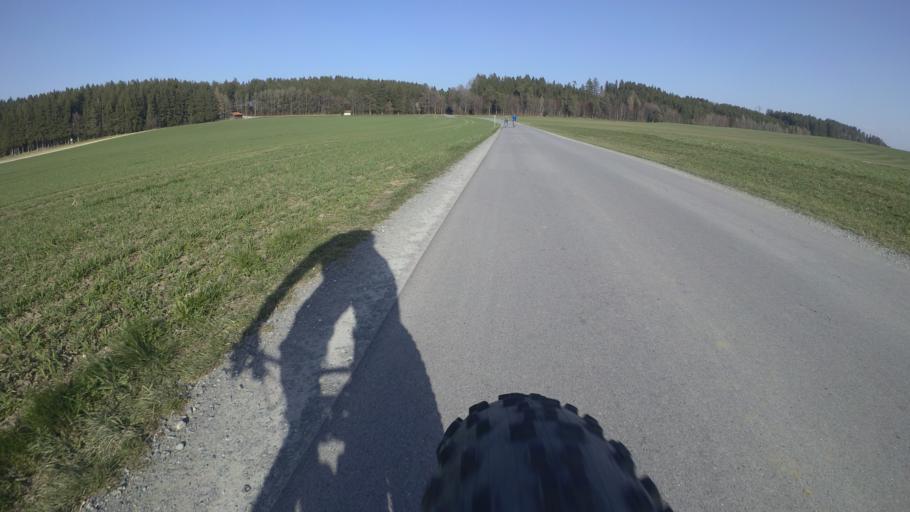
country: DE
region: Bavaria
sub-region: Upper Bavaria
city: Traunreut
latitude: 47.9399
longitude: 12.5592
